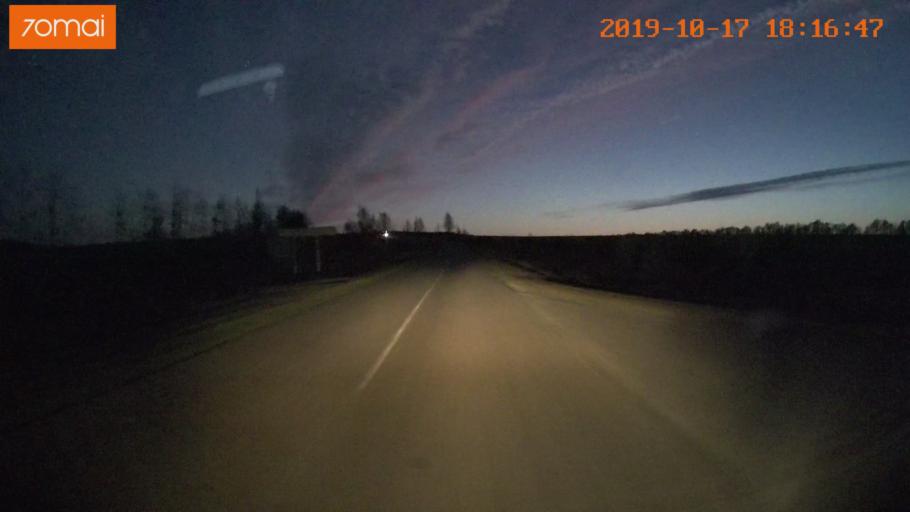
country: RU
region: Tula
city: Kurkino
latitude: 53.3962
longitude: 38.5113
